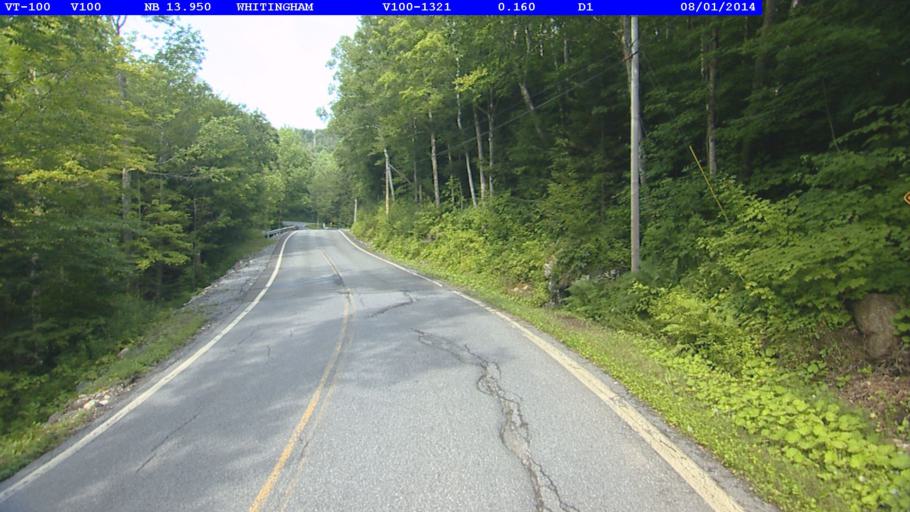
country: US
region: Massachusetts
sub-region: Franklin County
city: Charlemont
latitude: 42.7675
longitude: -72.9260
